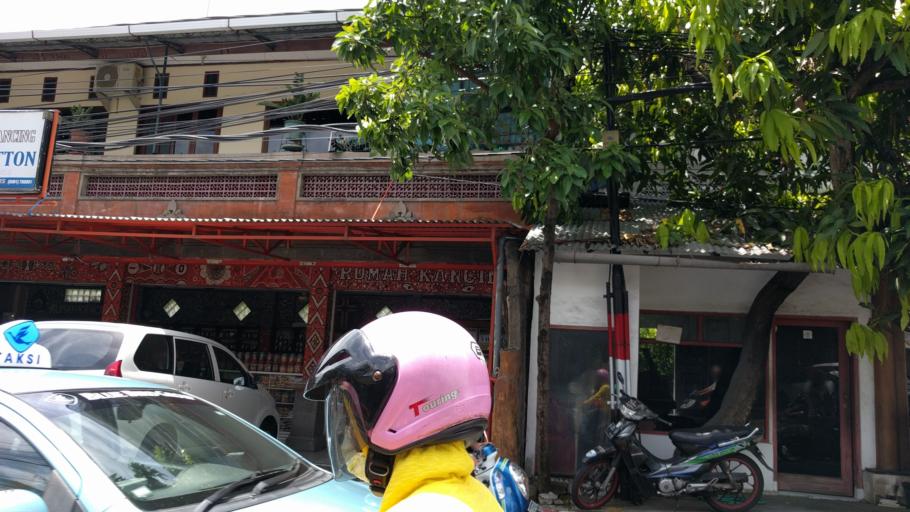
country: ID
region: Bali
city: Kuta
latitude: -8.6721
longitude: 115.1660
